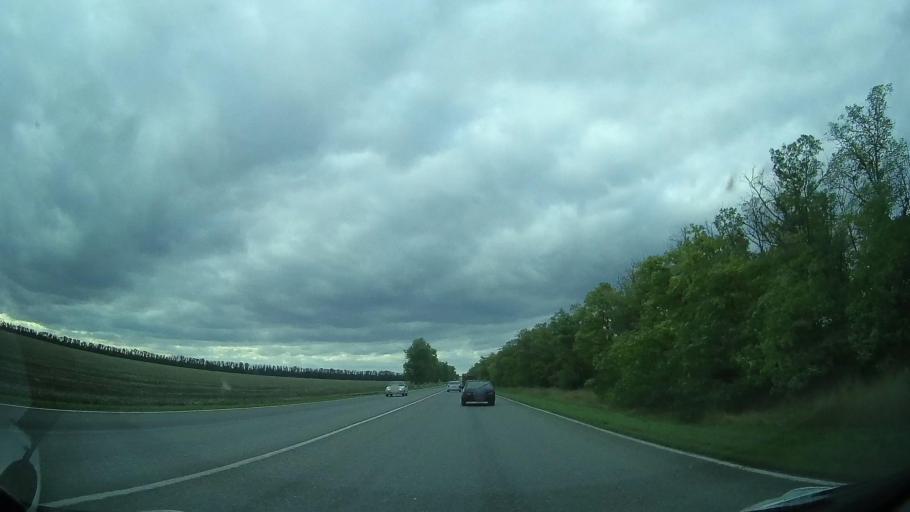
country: RU
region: Rostov
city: Zernograd
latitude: 46.8256
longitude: 40.2488
